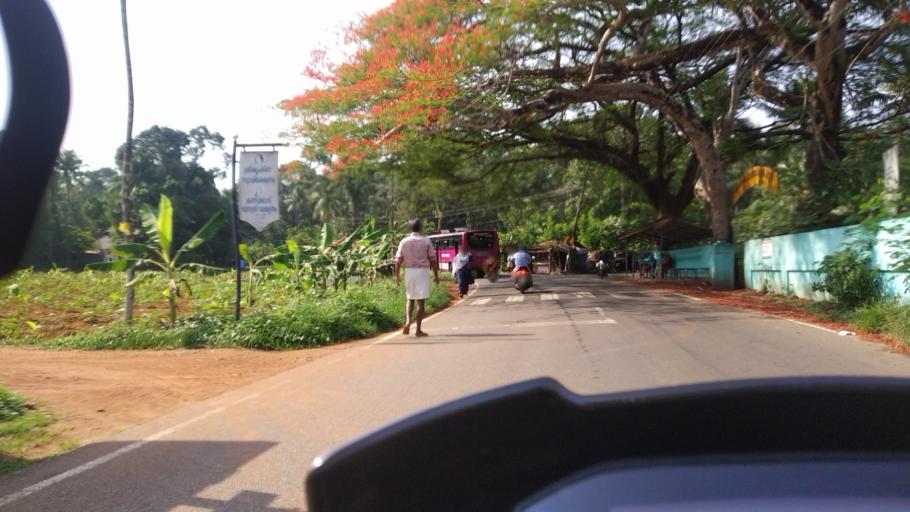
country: IN
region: Kerala
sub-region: Ernakulam
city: Piravam
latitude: 9.8198
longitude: 76.5525
